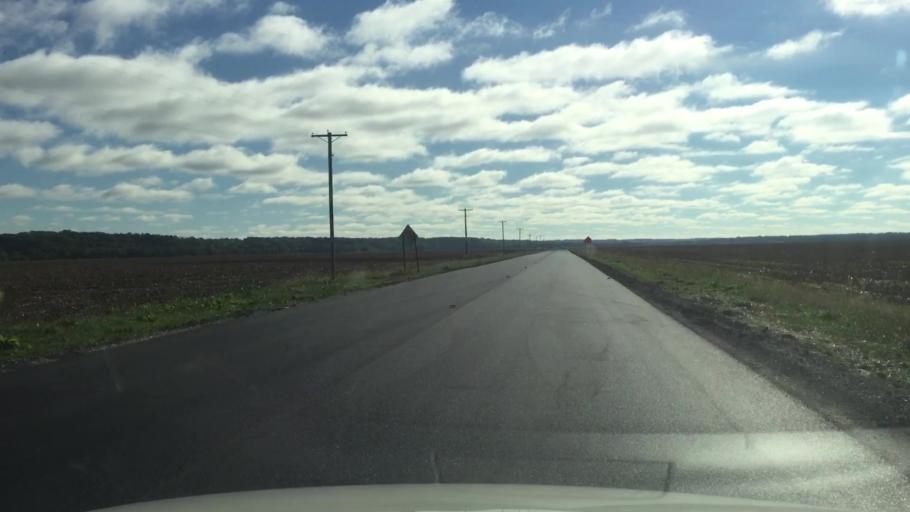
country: US
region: Missouri
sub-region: Howard County
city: New Franklin
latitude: 38.9961
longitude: -92.6638
